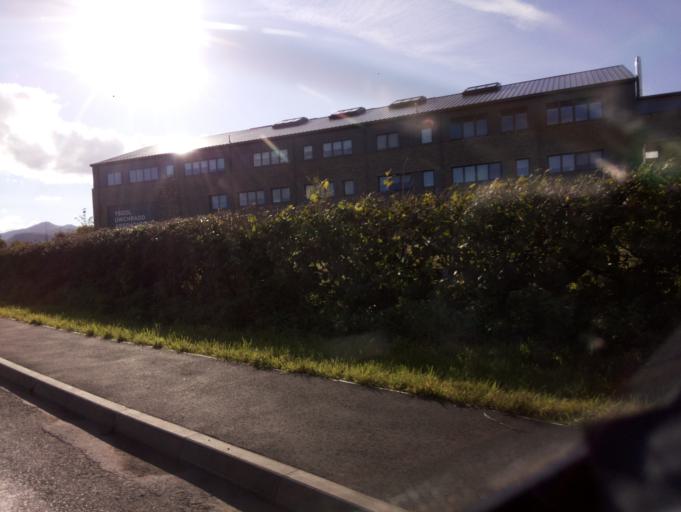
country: GB
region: Wales
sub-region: Sir Powys
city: Brecon
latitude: 51.9546
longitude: -3.3793
